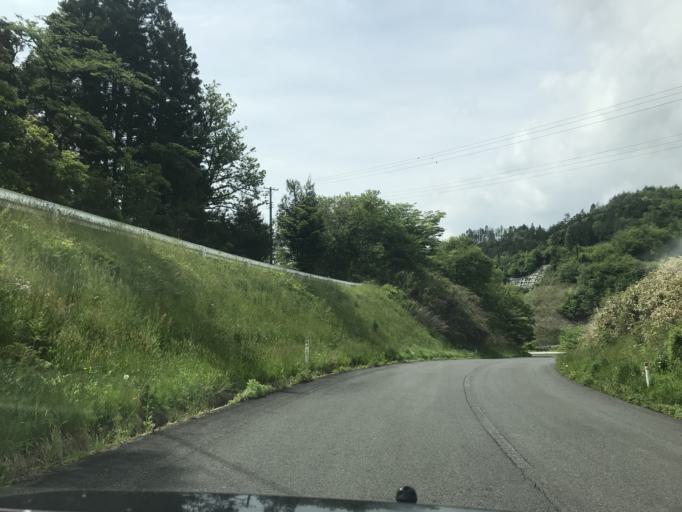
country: JP
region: Iwate
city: Ichinoseki
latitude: 38.8622
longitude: 140.9840
